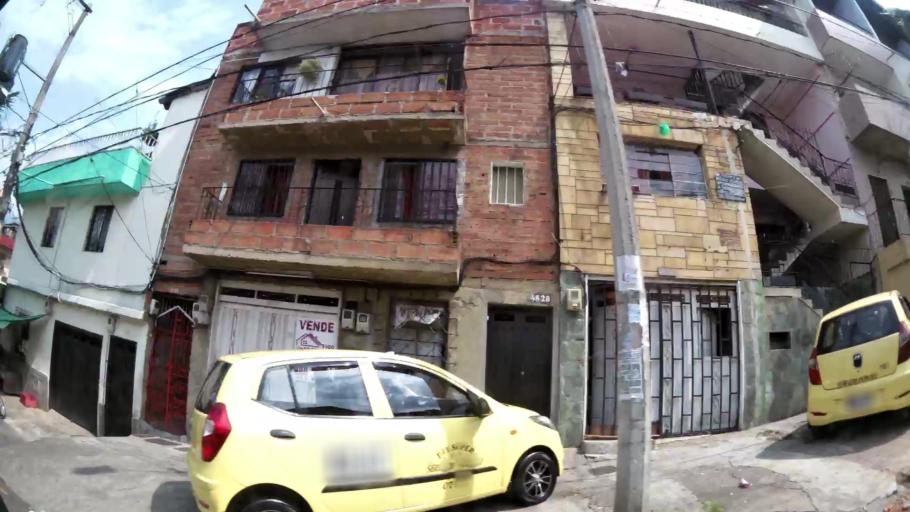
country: CO
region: Antioquia
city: Medellin
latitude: 6.2750
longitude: -75.5564
